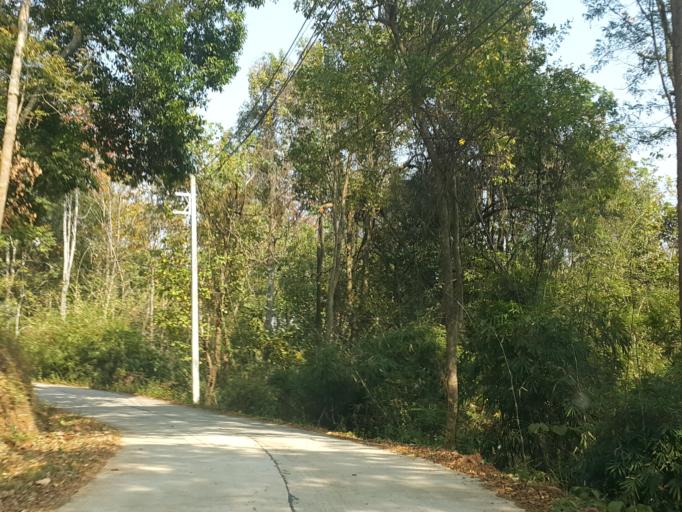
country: TH
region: Chiang Mai
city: Mae Taeng
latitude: 19.0171
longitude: 98.8025
